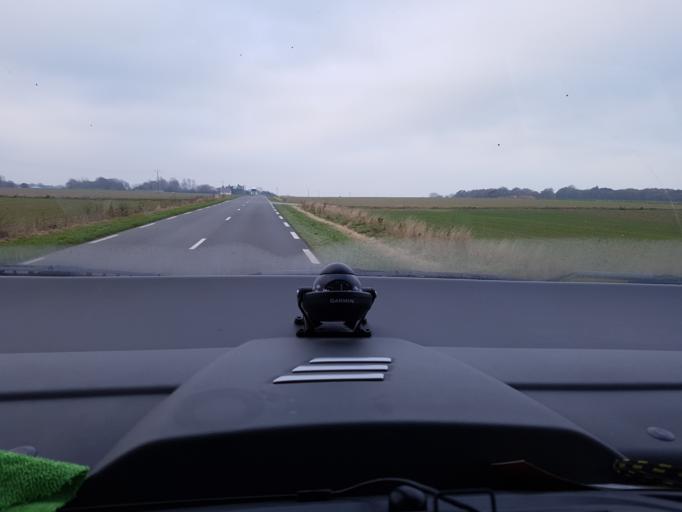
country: FR
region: Picardie
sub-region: Departement de la Somme
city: Ault
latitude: 50.0839
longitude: 1.4454
